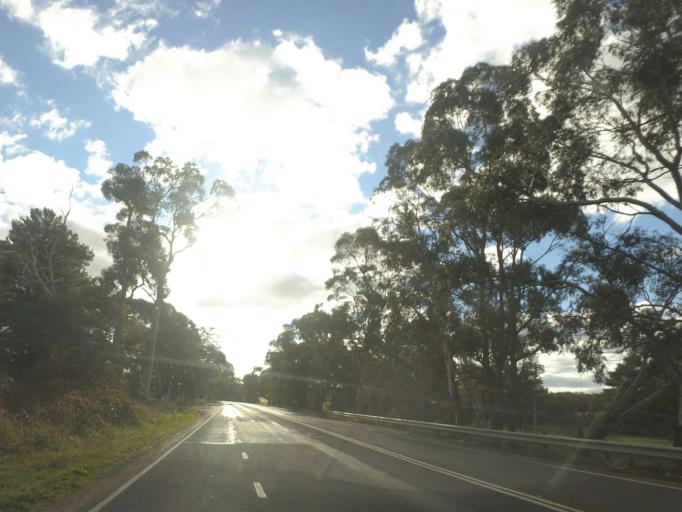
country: AU
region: Victoria
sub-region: Mount Alexander
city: Castlemaine
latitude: -37.1236
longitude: 144.3434
